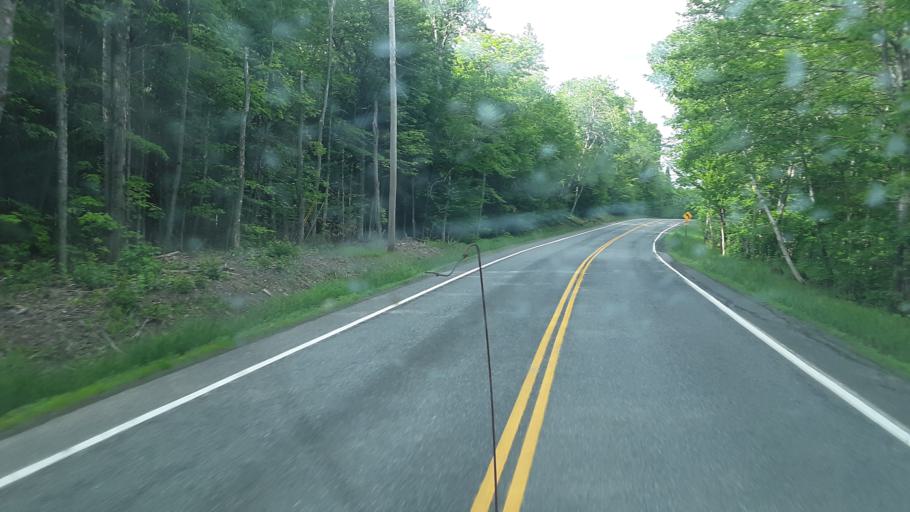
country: US
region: Maine
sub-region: Penobscot County
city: Patten
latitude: 46.1521
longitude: -68.3551
